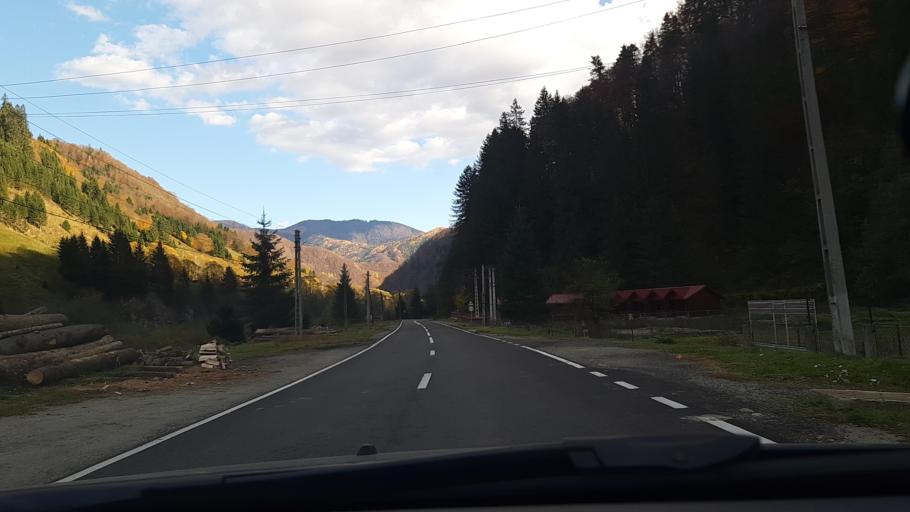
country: RO
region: Valcea
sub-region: Comuna Voineasa
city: Voineasa
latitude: 45.4106
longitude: 23.9667
